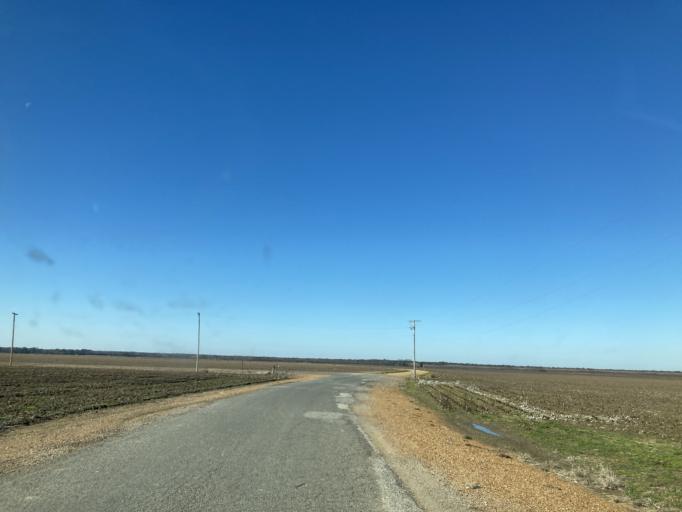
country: US
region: Mississippi
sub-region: Sharkey County
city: Rolling Fork
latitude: 32.8212
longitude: -90.7280
